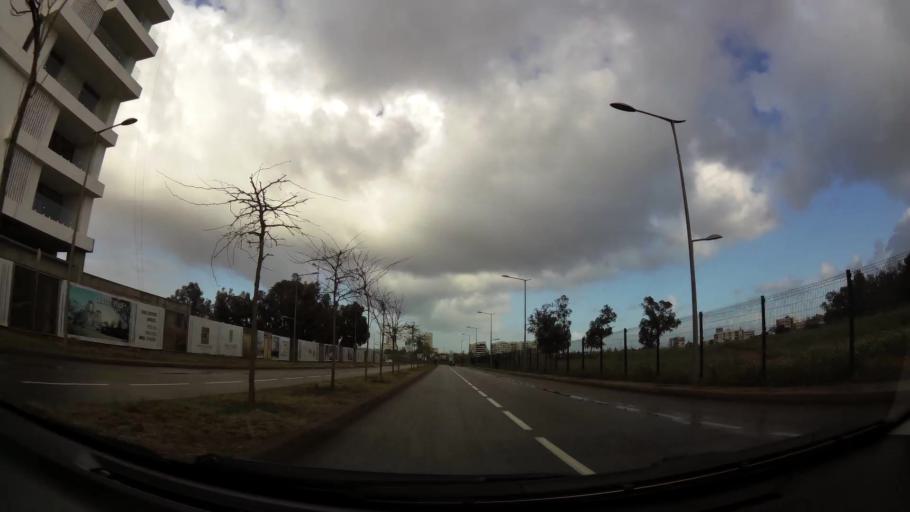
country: MA
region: Grand Casablanca
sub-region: Casablanca
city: Casablanca
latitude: 33.5622
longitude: -7.6533
